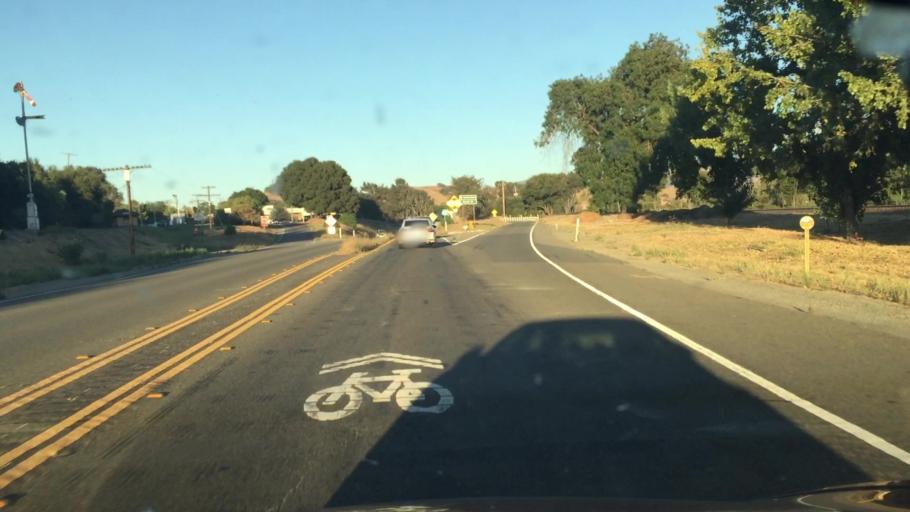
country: US
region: California
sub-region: Alameda County
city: Pleasanton
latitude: 37.5936
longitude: -121.8922
